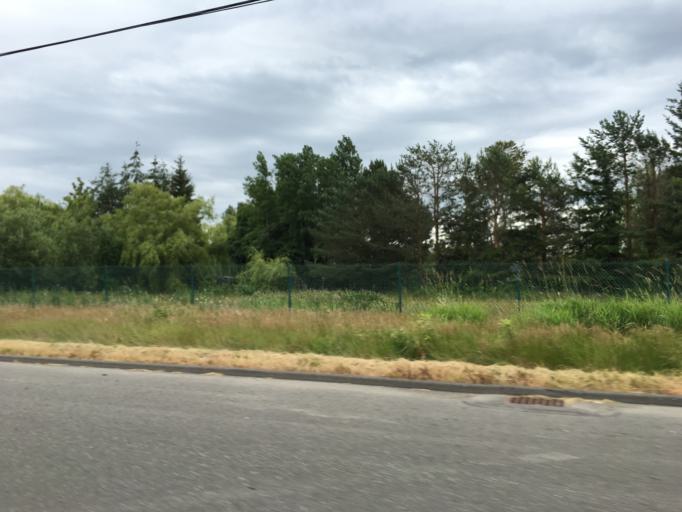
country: US
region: Washington
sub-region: Whatcom County
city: Bellingham
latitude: 48.8190
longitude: -122.4859
